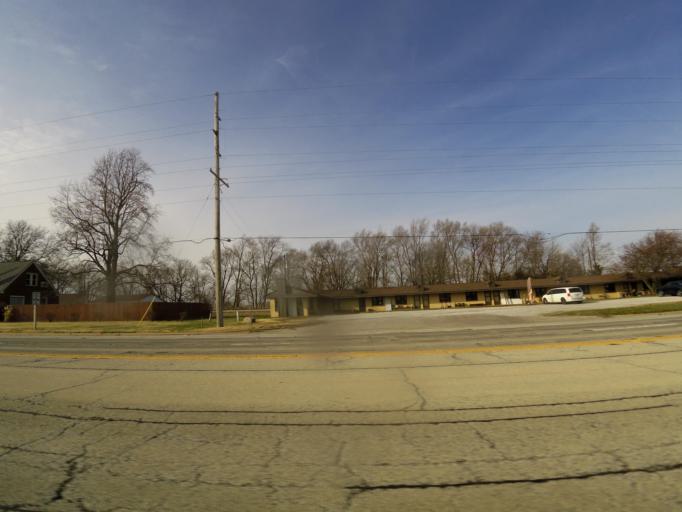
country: US
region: Illinois
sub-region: Macon County
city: Macon
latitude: 39.7774
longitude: -88.9797
